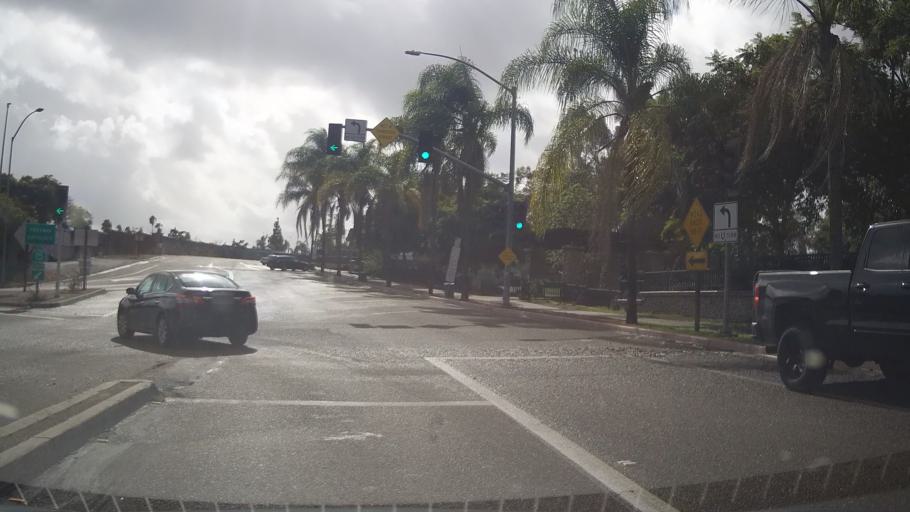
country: US
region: California
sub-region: San Diego County
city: San Diego
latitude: 32.7627
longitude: -117.1101
